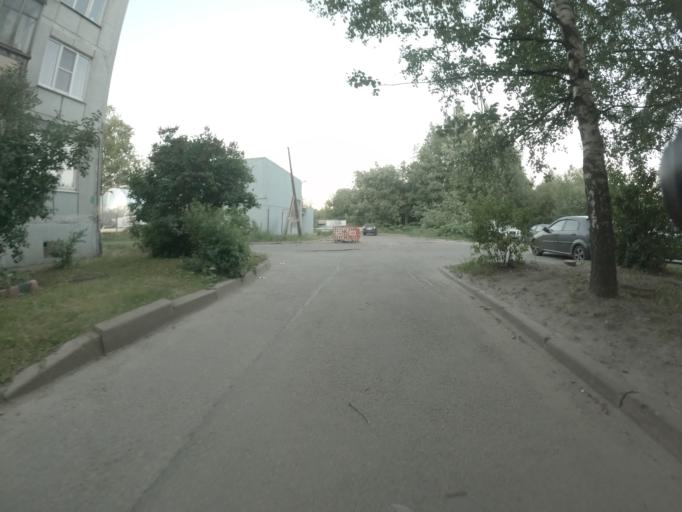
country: RU
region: St.-Petersburg
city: Krasnogvargeisky
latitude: 59.9841
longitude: 30.5202
